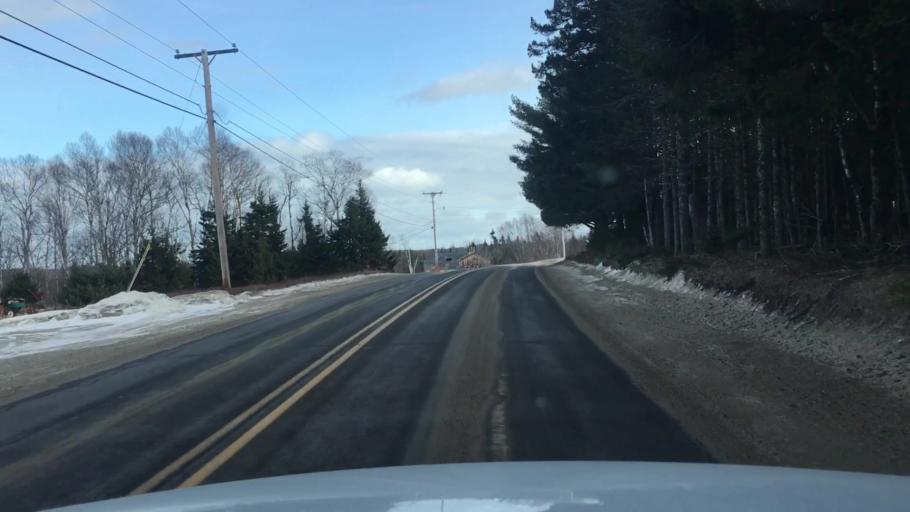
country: US
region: Maine
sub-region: Washington County
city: Jonesport
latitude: 44.6085
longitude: -67.5986
